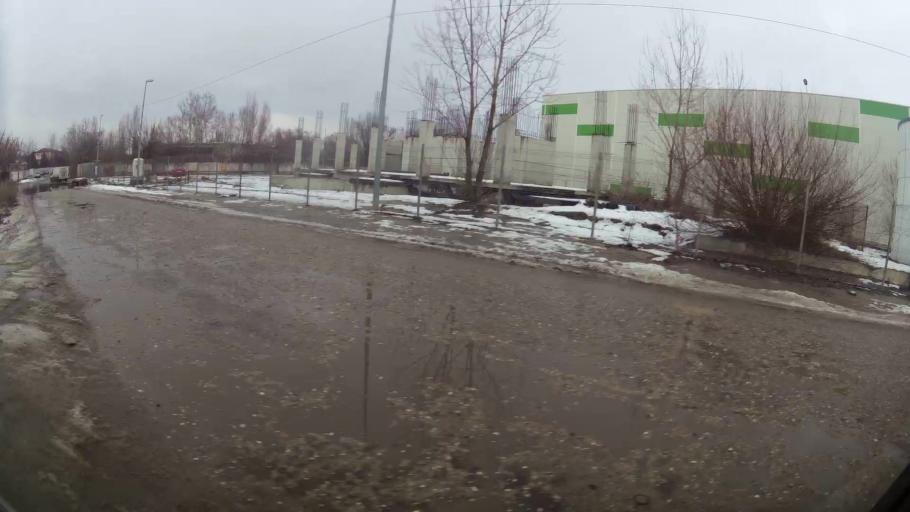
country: RO
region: Ilfov
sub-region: Comuna Glina
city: Catelu
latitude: 44.3994
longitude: 26.2019
